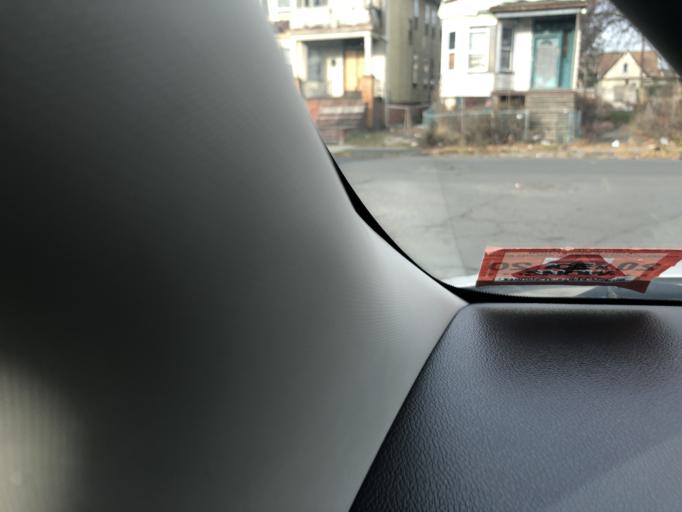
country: US
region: New Jersey
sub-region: Essex County
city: Irvington
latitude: 40.7274
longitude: -74.2178
